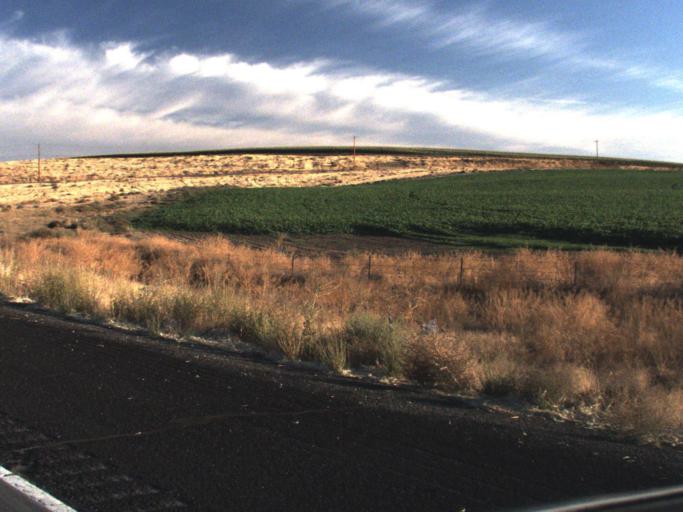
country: US
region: Washington
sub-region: Franklin County
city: Pasco
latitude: 46.2826
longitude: -119.0926
